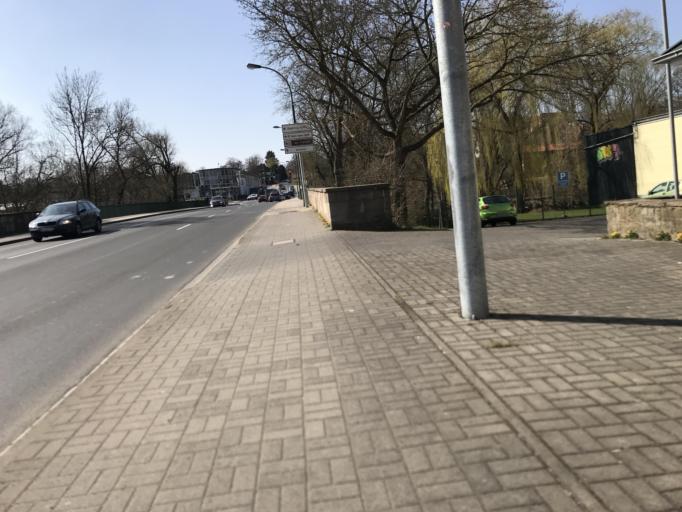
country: DE
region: Hesse
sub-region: Regierungsbezirk Kassel
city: Fulda
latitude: 50.5549
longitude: 9.6655
